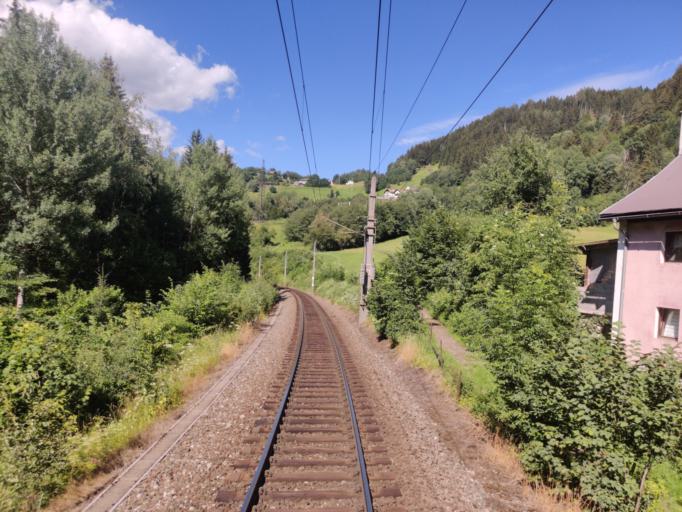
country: AT
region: Tyrol
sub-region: Politischer Bezirk Landeck
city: Tobadill
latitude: 47.1169
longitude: 10.4936
